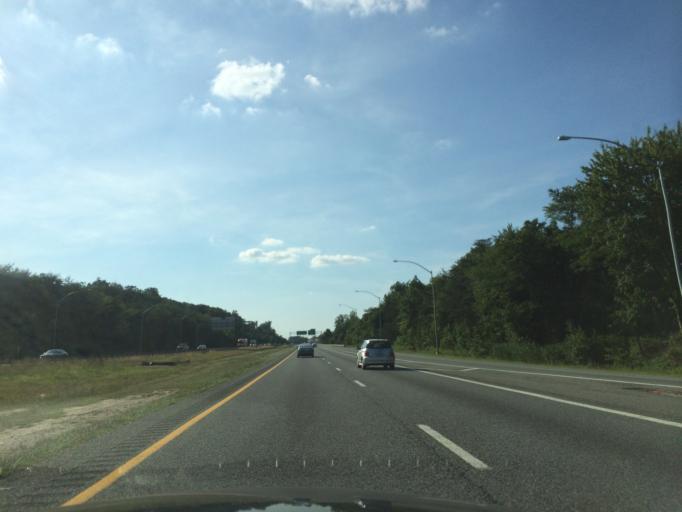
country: US
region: Maryland
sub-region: Howard County
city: West Elkridge
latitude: 39.1997
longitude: -76.7694
